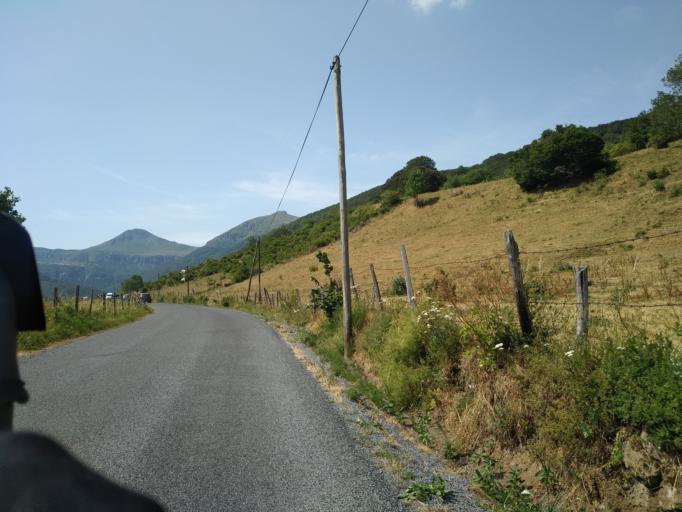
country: FR
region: Auvergne
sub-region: Departement du Cantal
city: Riom-es-Montagnes
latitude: 45.1514
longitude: 2.7002
